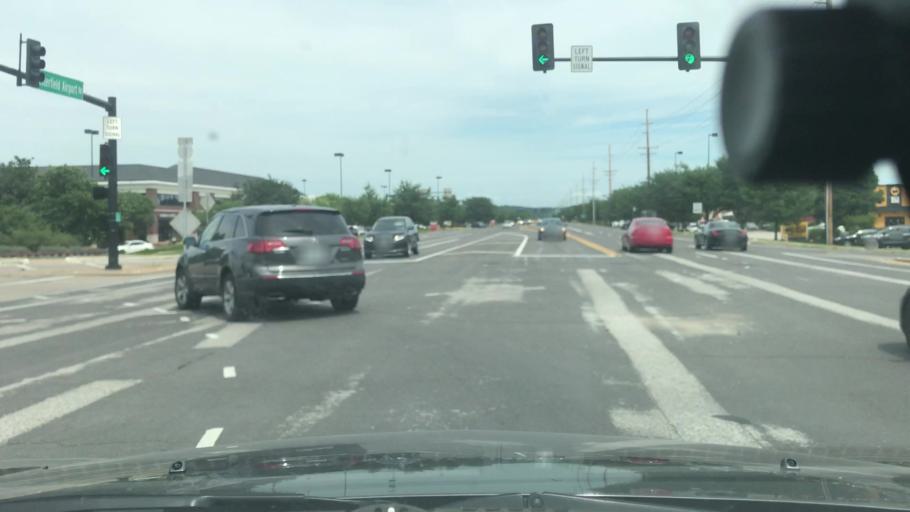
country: US
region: Missouri
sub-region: Saint Louis County
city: Chesterfield
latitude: 38.6684
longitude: -90.6000
